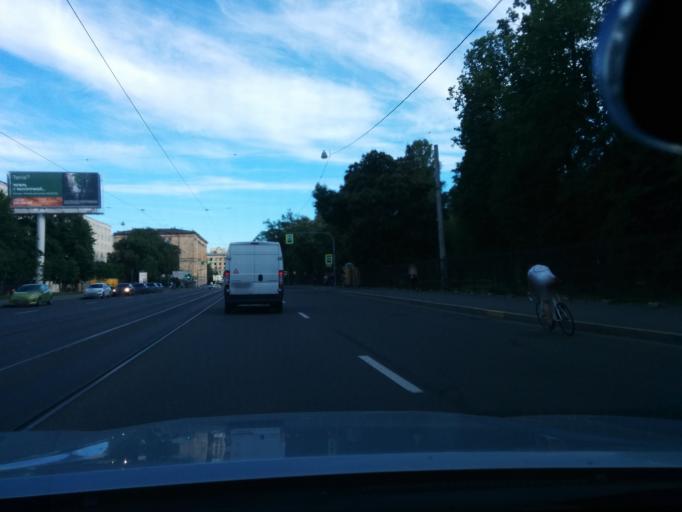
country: RU
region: Leningrad
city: Svetlanovskiy
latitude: 60.0070
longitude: 30.3262
